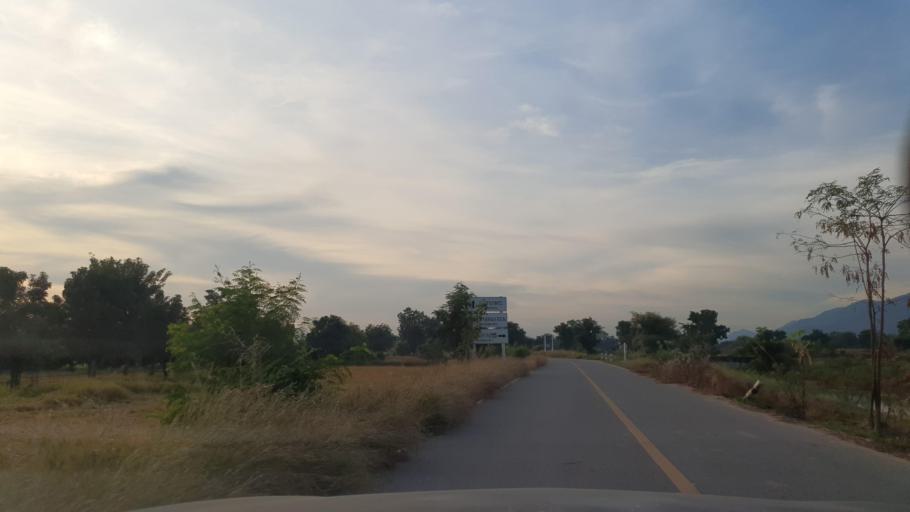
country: TH
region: Uthai Thani
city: Sawang Arom
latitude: 15.7113
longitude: 99.9572
